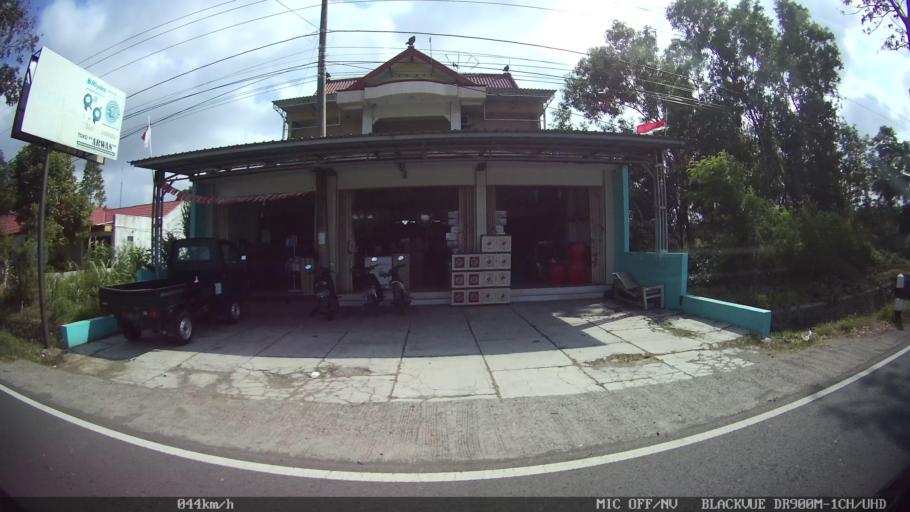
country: ID
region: Daerah Istimewa Yogyakarta
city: Srandakan
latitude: -7.8927
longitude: 110.1340
